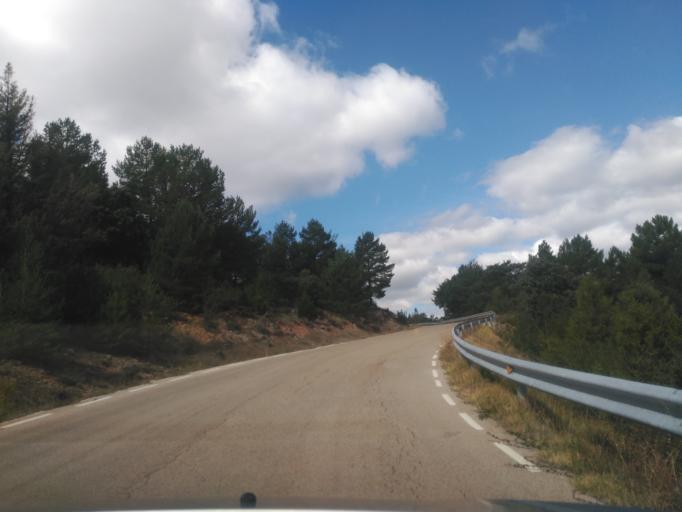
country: ES
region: Castille and Leon
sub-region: Provincia de Soria
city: Espejon
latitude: 41.8407
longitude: -3.2382
